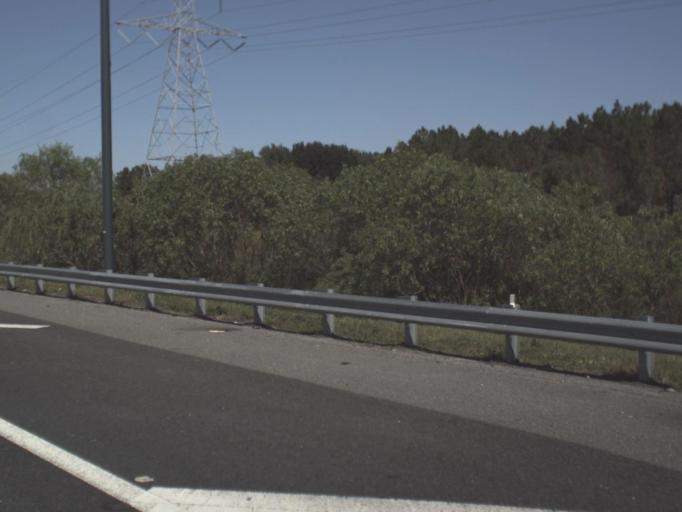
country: US
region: Florida
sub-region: Lake County
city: Hawthorne
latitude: 28.7570
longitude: -81.9403
